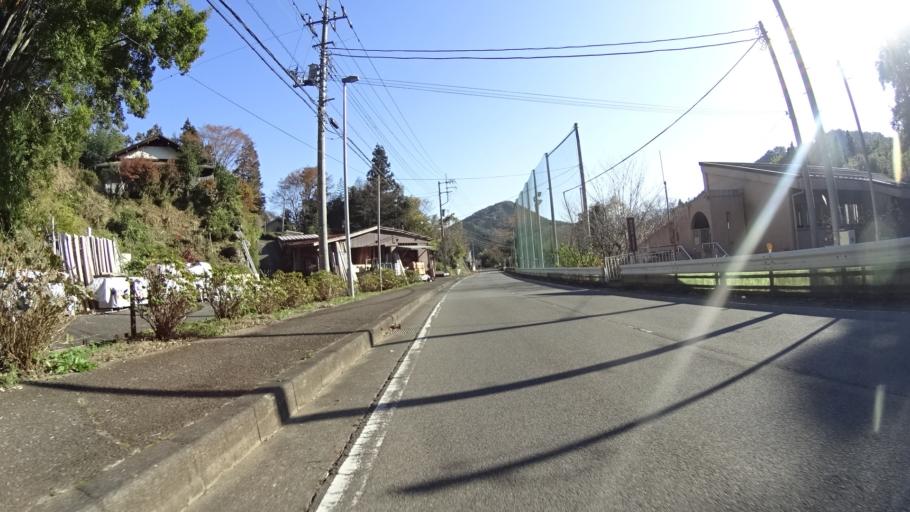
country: JP
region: Yamanashi
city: Uenohara
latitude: 35.6466
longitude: 139.1246
